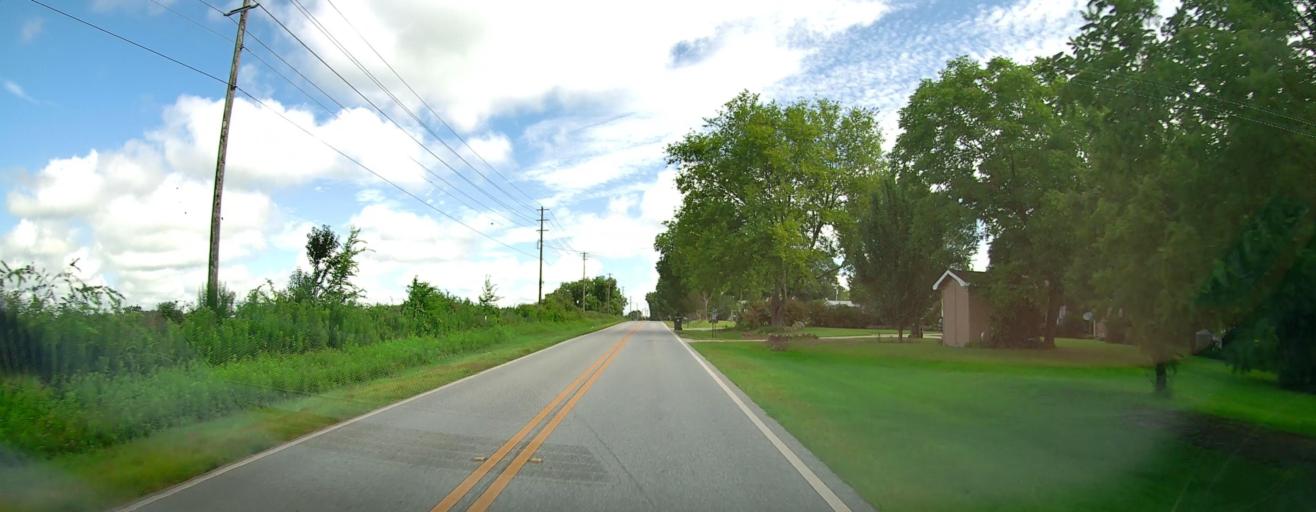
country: US
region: Georgia
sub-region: Peach County
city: Byron
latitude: 32.6108
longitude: -83.7955
